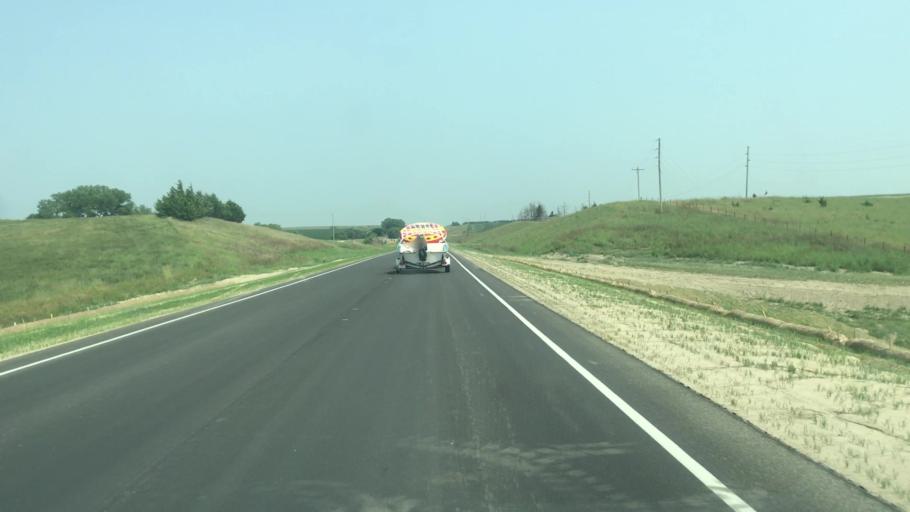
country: US
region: Nebraska
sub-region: Sherman County
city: Loup City
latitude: 41.2635
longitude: -98.9224
